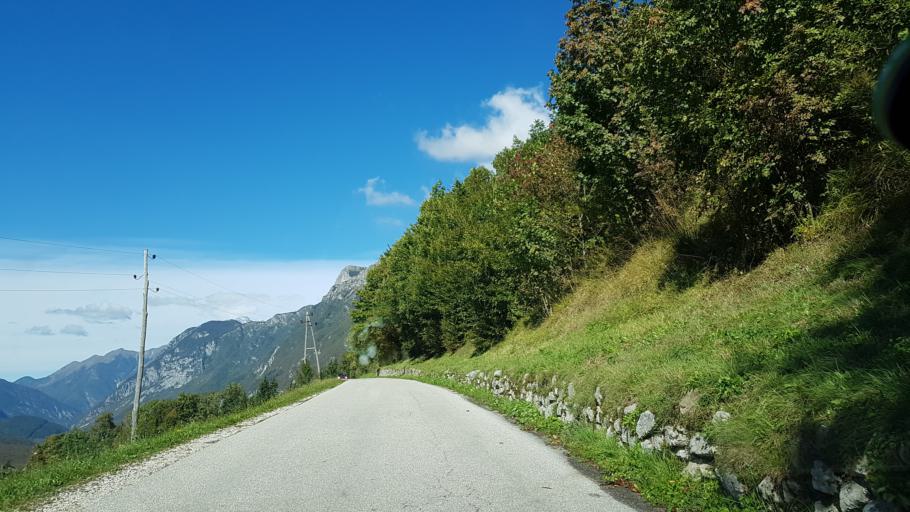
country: SI
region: Kobarid
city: Kobarid
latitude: 46.2617
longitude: 13.6113
